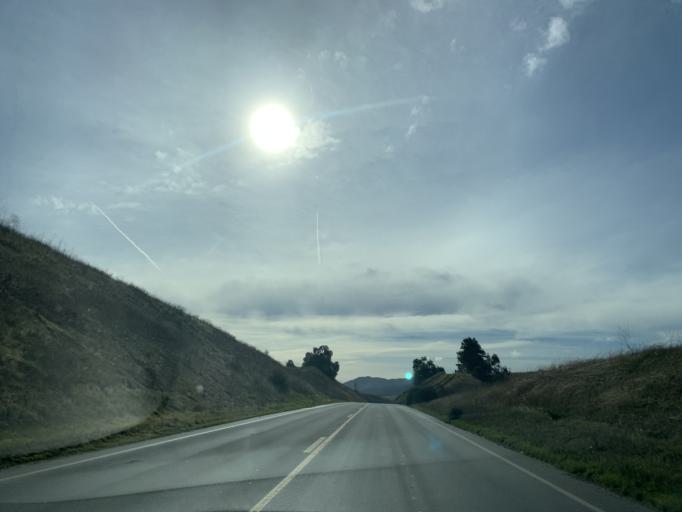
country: US
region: California
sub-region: San Benito County
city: Ridgemark
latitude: 36.7182
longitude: -121.2780
